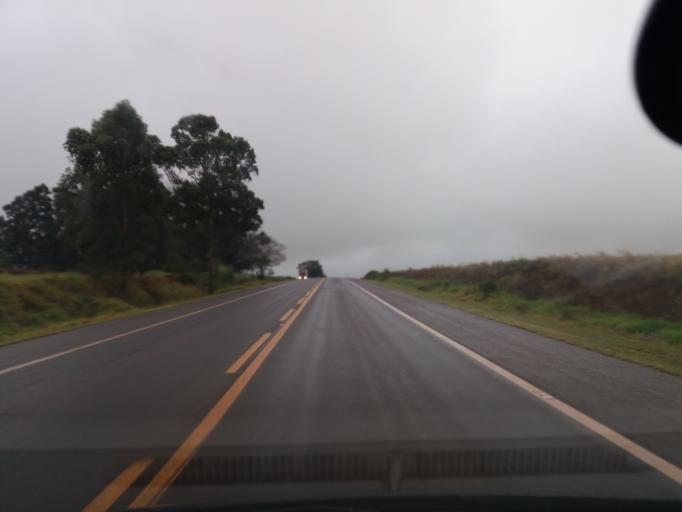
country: BR
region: Parana
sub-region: Campo Mourao
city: Campo Mourao
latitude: -24.2989
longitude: -52.5876
